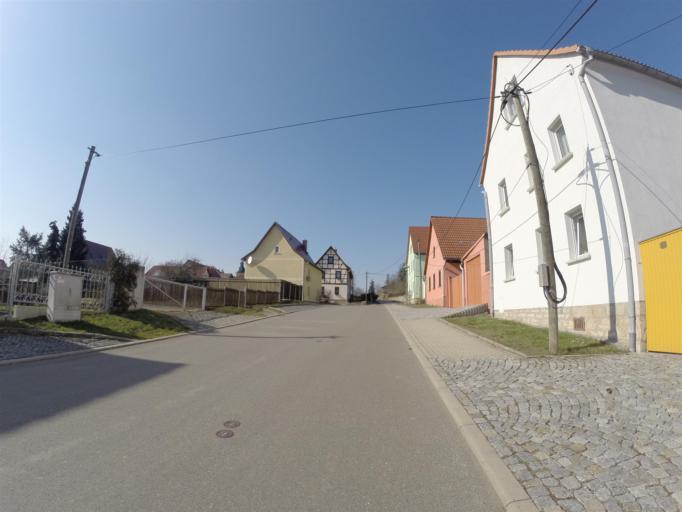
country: DE
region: Thuringia
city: Mellingen
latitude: 50.9420
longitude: 11.3976
